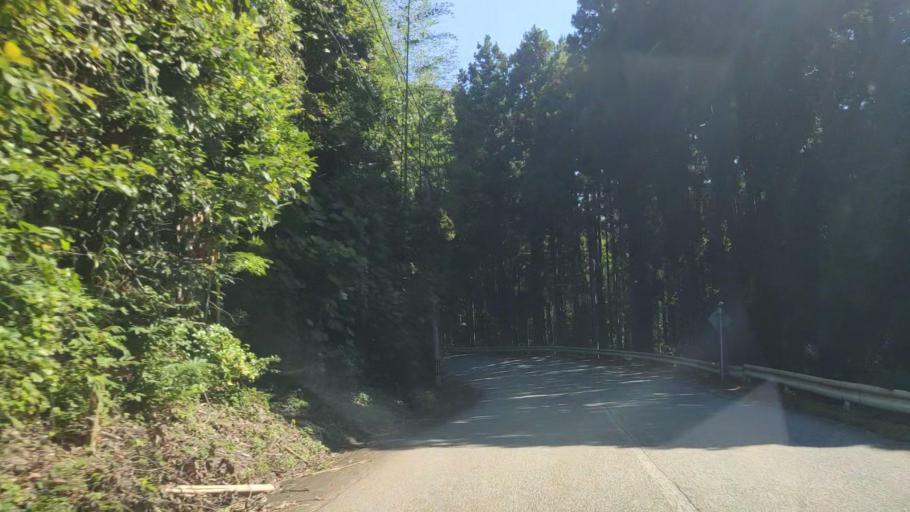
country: JP
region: Ishikawa
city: Nanao
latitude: 37.5094
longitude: 137.3374
